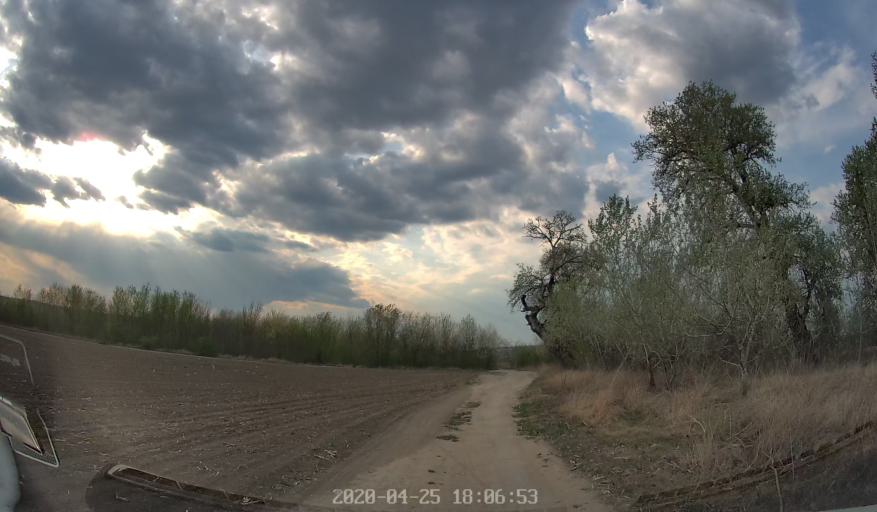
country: MD
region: Chisinau
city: Vadul lui Voda
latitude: 47.1284
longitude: 29.0838
